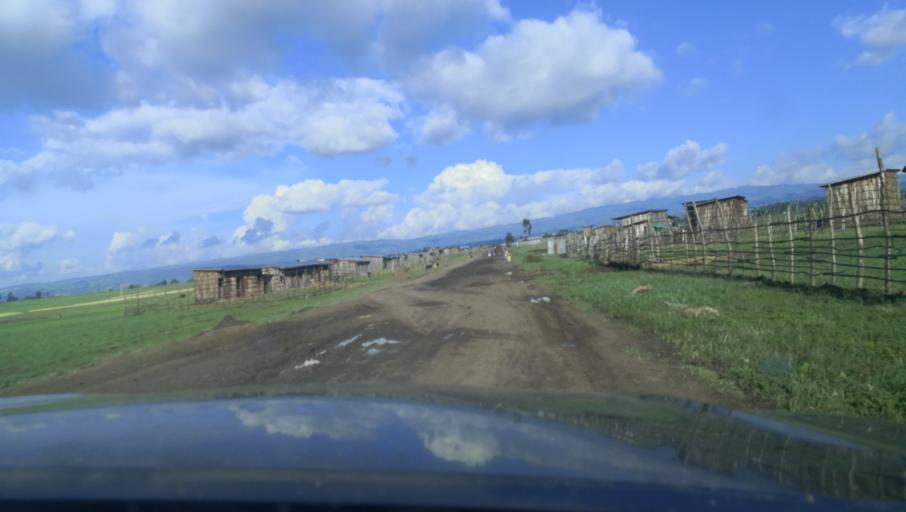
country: ET
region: Oromiya
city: Tulu Bolo
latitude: 8.4761
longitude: 38.2385
